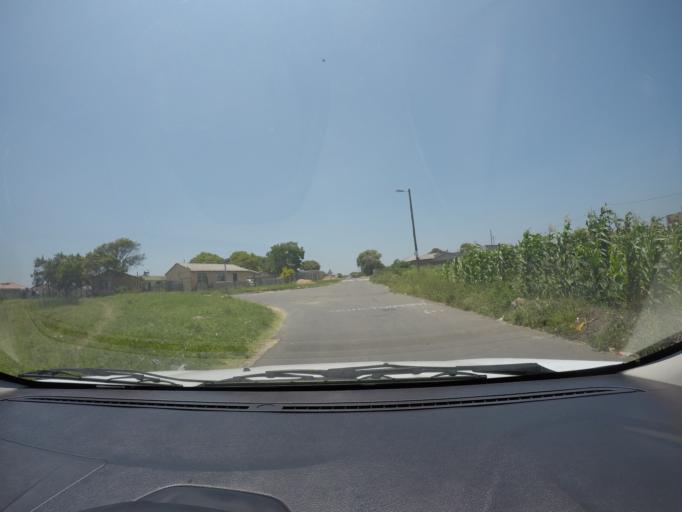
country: ZA
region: KwaZulu-Natal
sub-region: uThungulu District Municipality
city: eSikhawini
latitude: -28.8846
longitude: 31.9010
